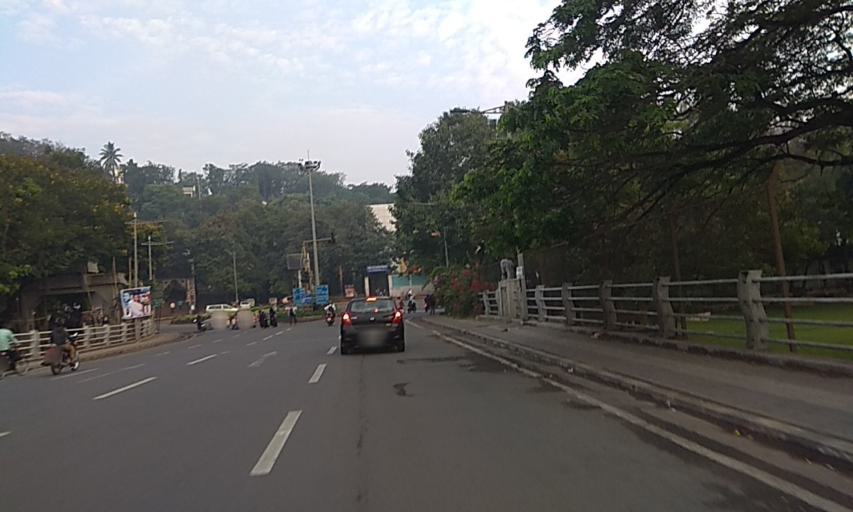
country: IN
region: Maharashtra
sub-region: Pune Division
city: Shivaji Nagar
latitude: 18.5444
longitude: 73.8834
